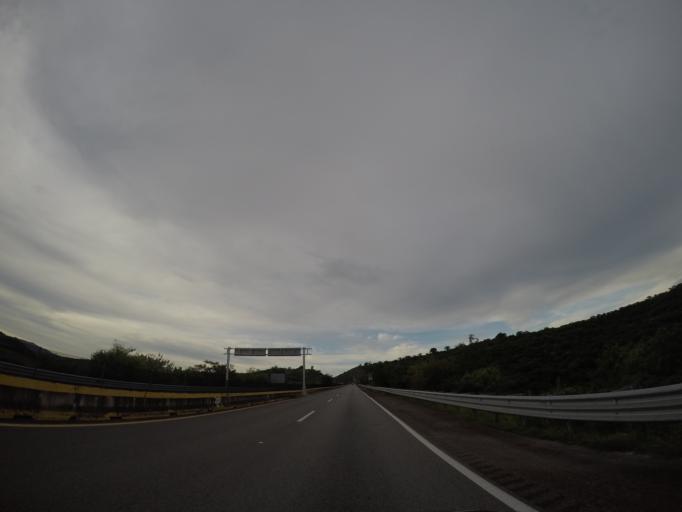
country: MX
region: Guerrero
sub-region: Huitzuco de los Figueroa
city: San Francisco Ozomatlan
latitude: 18.0220
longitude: -99.2720
